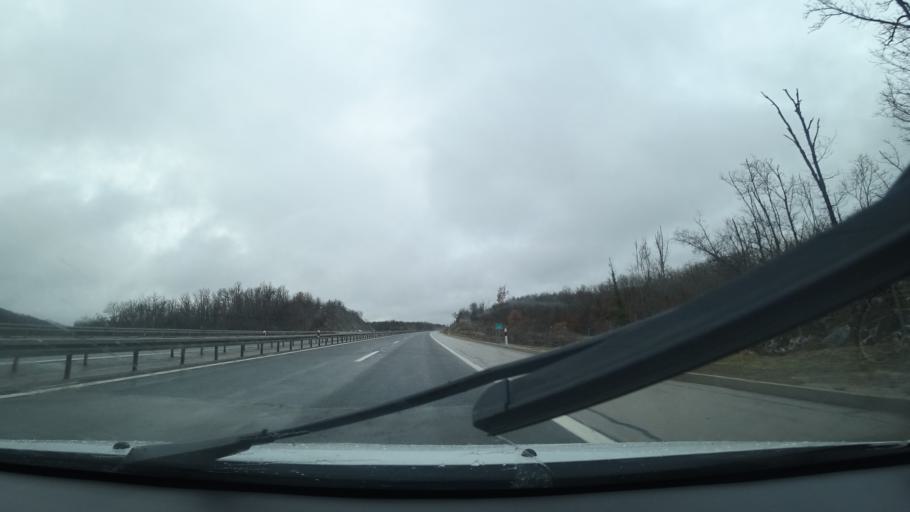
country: HR
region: Licko-Senjska
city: Gospic
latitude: 44.7021
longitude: 15.3942
